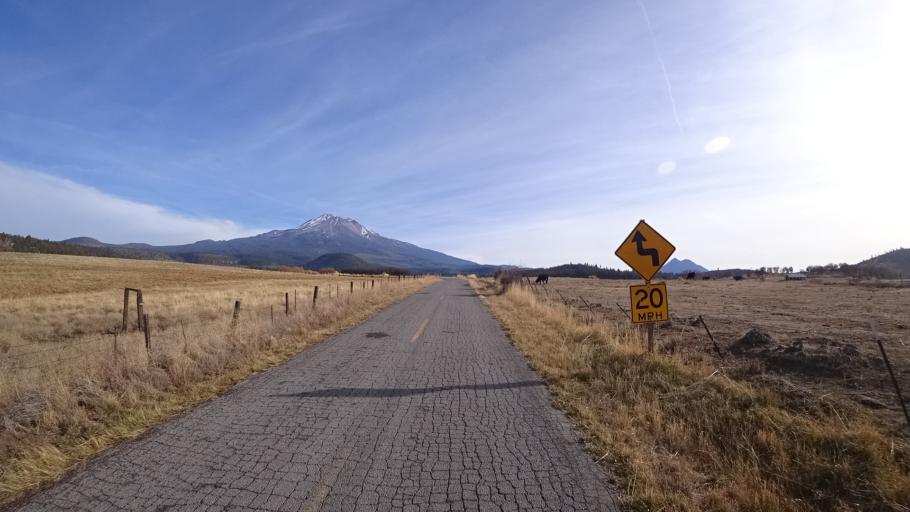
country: US
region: California
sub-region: Siskiyou County
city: Weed
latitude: 41.4622
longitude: -122.3861
